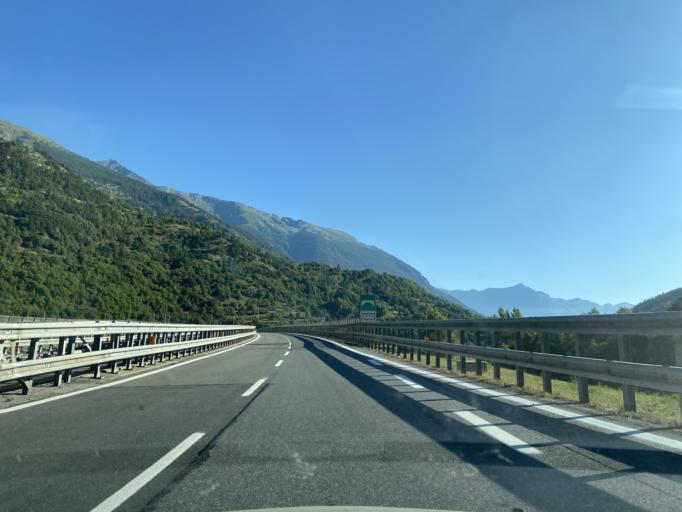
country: IT
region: Piedmont
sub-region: Provincia di Torino
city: Salbertrand
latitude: 45.0728
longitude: 6.8936
